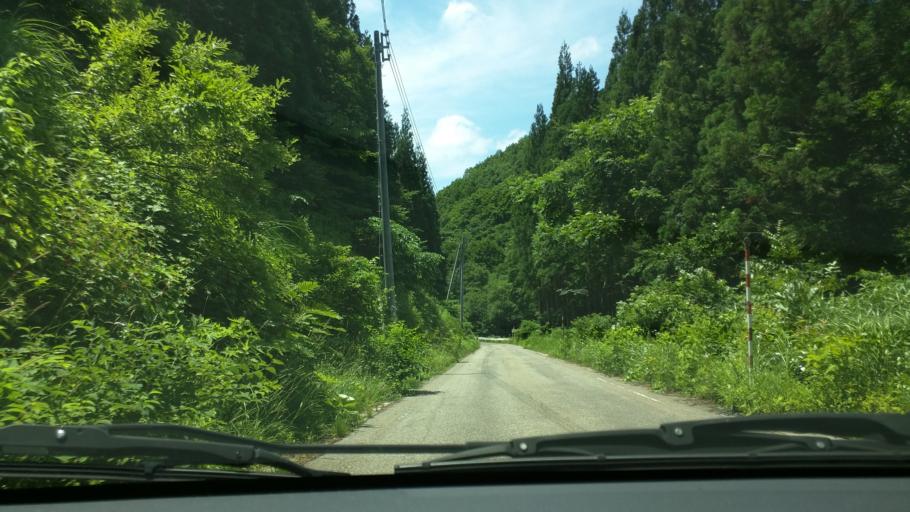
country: JP
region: Fukushima
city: Kitakata
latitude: 37.2554
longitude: 139.7458
